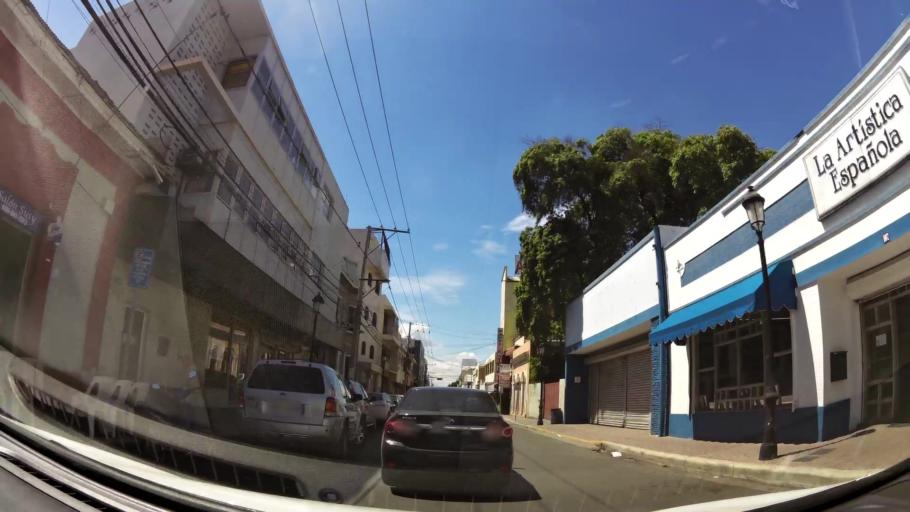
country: DO
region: Santiago
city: Santiago de los Caballeros
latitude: 19.4528
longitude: -70.7049
